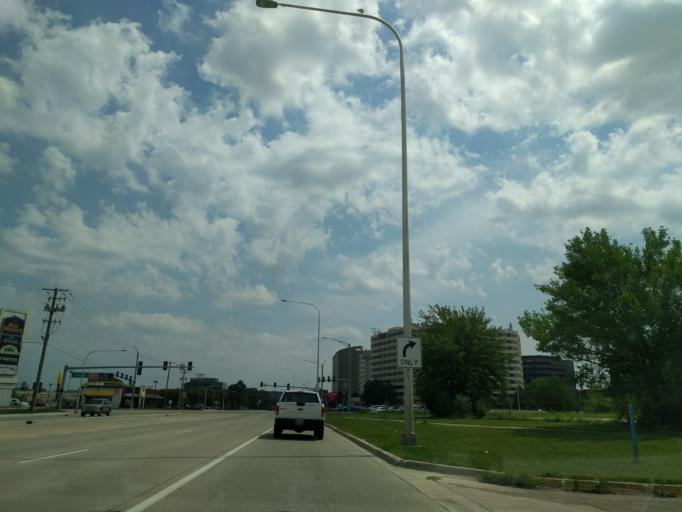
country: US
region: Illinois
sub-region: Cook County
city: Rosemont
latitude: 41.9984
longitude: -87.8859
